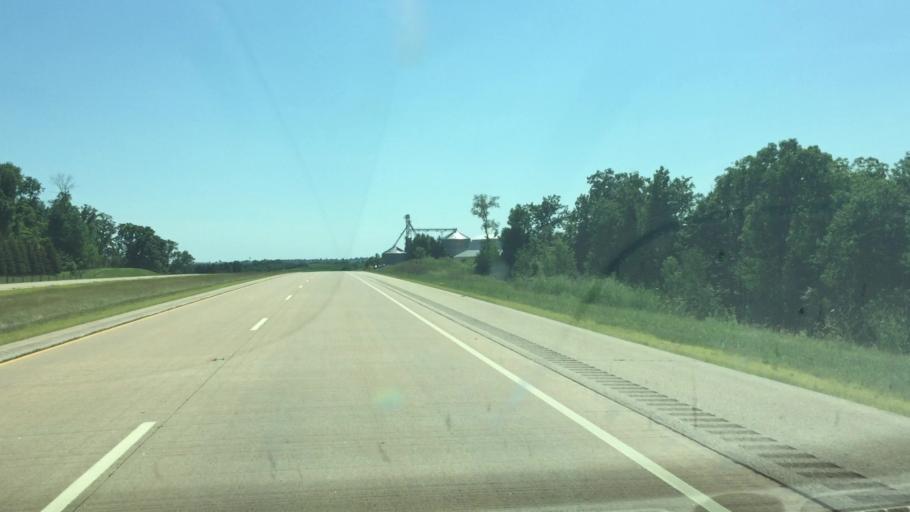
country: US
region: Wisconsin
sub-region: Grant County
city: Dickeyville
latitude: 42.6785
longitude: -90.5420
